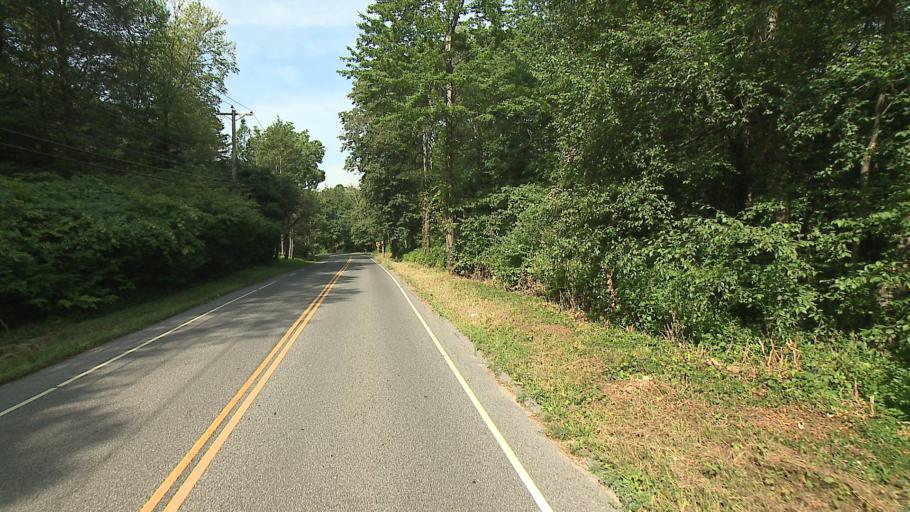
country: US
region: Connecticut
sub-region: Fairfield County
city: Sherman
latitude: 41.5893
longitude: -73.4774
